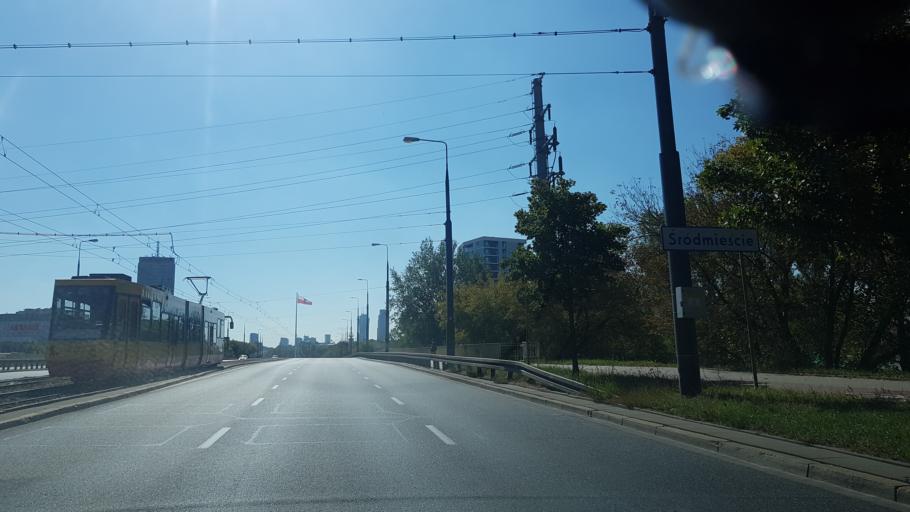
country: PL
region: Masovian Voivodeship
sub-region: Warszawa
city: Zoliborz
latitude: 52.2603
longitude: 20.9807
